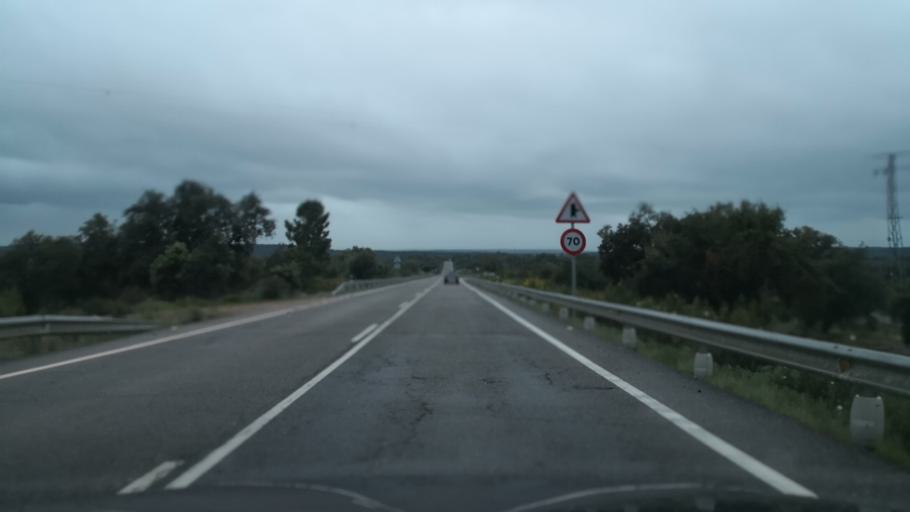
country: ES
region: Extremadura
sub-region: Provincia de Badajoz
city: Puebla de Obando
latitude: 39.1604
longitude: -6.6420
